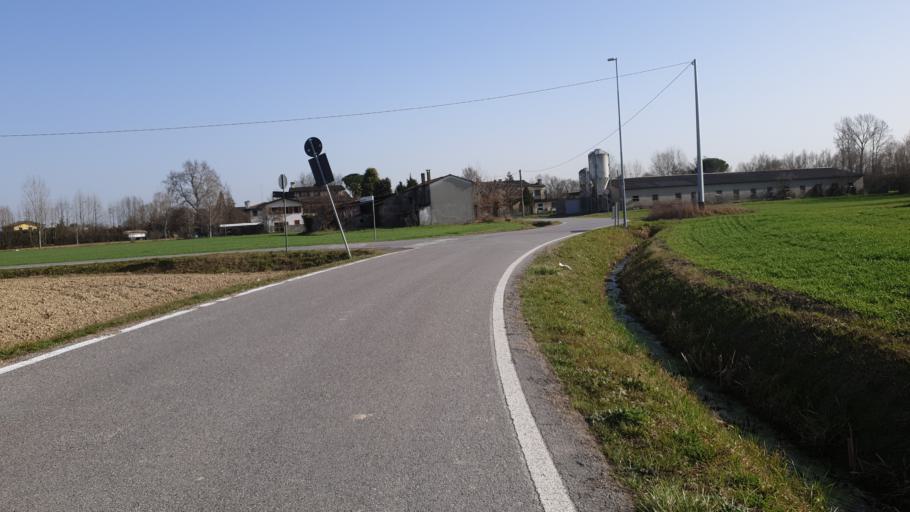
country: IT
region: Veneto
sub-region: Provincia di Padova
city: Vigodarzere
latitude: 45.4744
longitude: 11.8897
